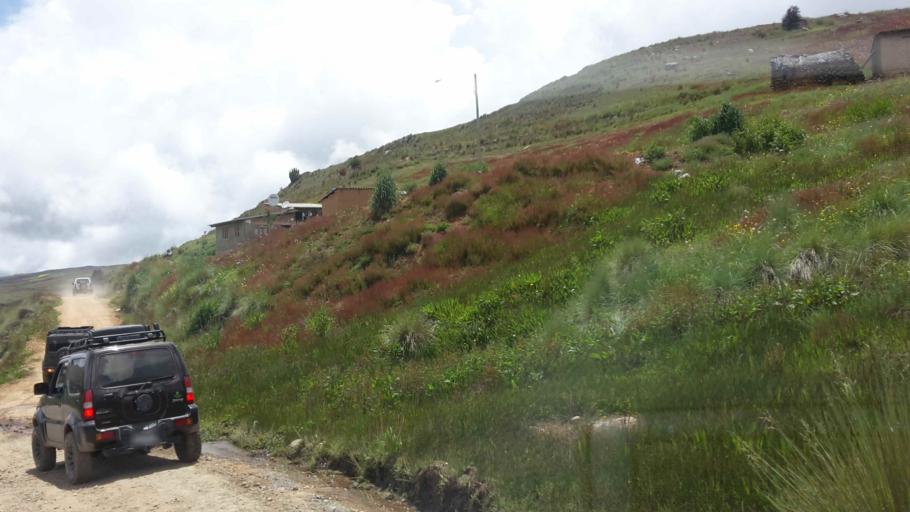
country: BO
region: Cochabamba
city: Cochabamba
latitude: -17.1885
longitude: -66.0743
